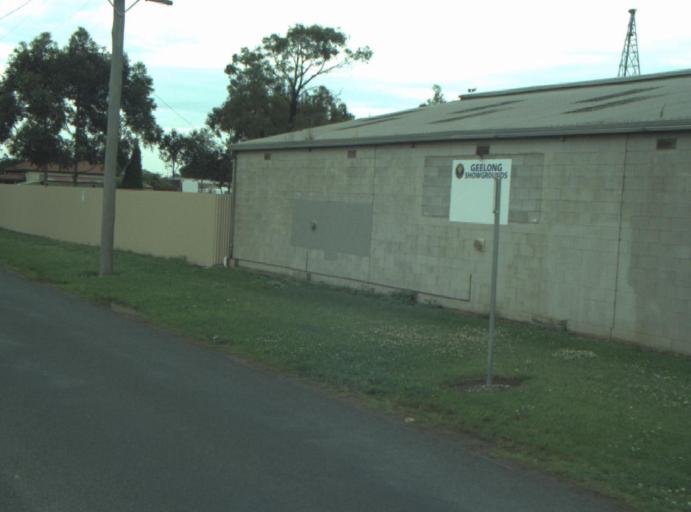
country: AU
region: Victoria
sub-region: Greater Geelong
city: Breakwater
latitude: -38.1723
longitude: 144.3720
